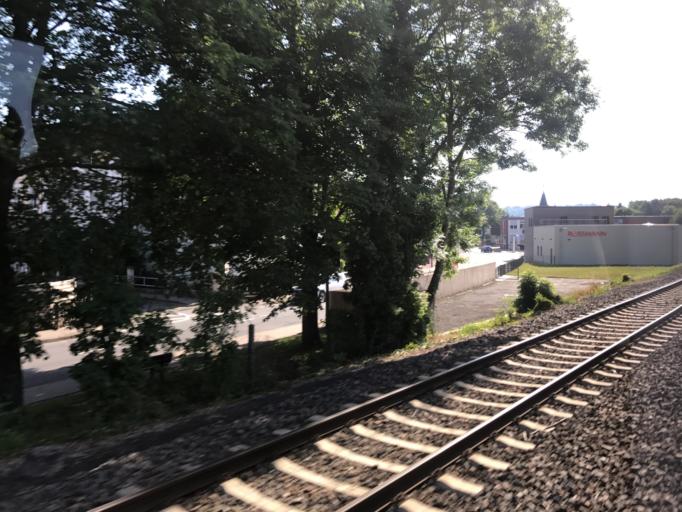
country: DE
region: Rheinland-Pfalz
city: Staudernheim
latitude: 49.7827
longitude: 7.6523
